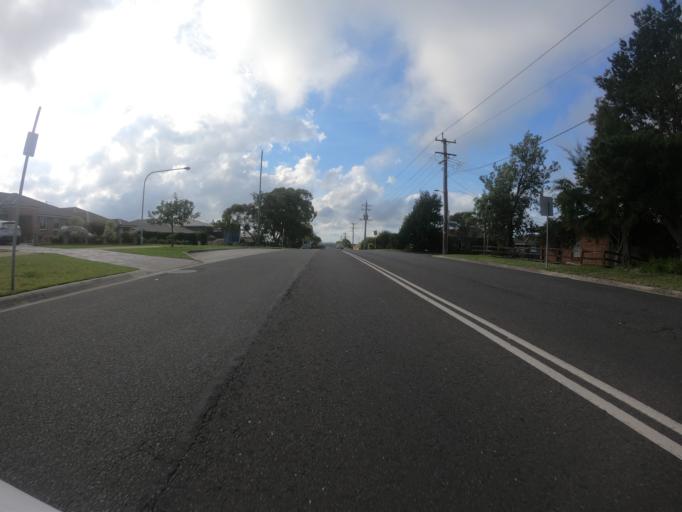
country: AU
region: New South Wales
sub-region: Wollongong
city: Helensburgh
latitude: -34.2012
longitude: 150.9799
